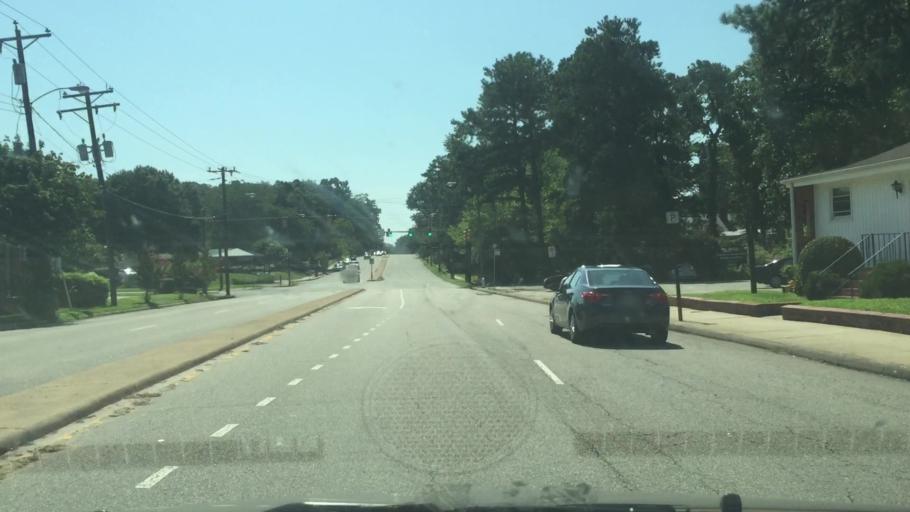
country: US
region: Virginia
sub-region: Henrico County
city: Dumbarton
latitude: 37.5763
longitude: -77.5093
